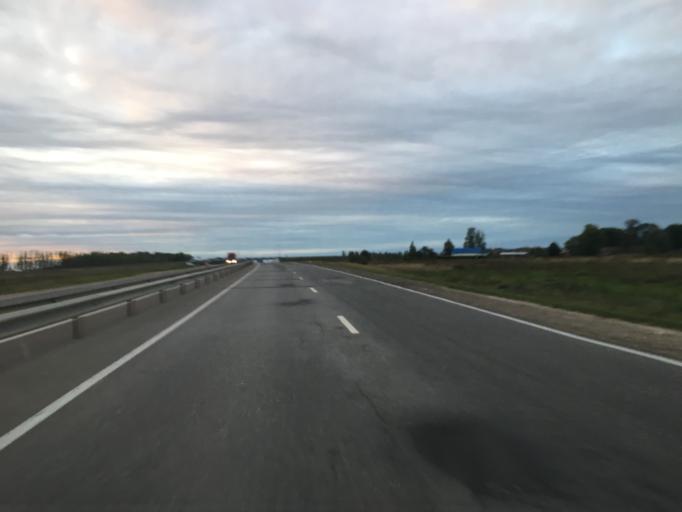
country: RU
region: Kaluga
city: Kaluga
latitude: 54.6205
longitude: 36.2941
